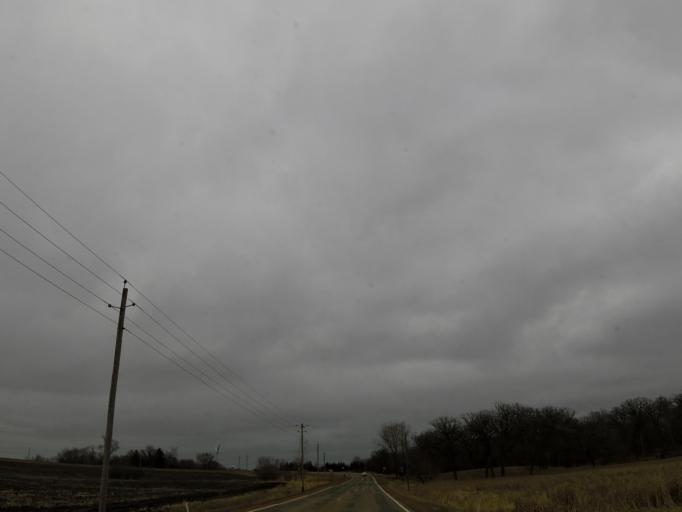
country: US
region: Minnesota
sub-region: Scott County
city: Shakopee
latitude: 44.7322
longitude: -93.5019
